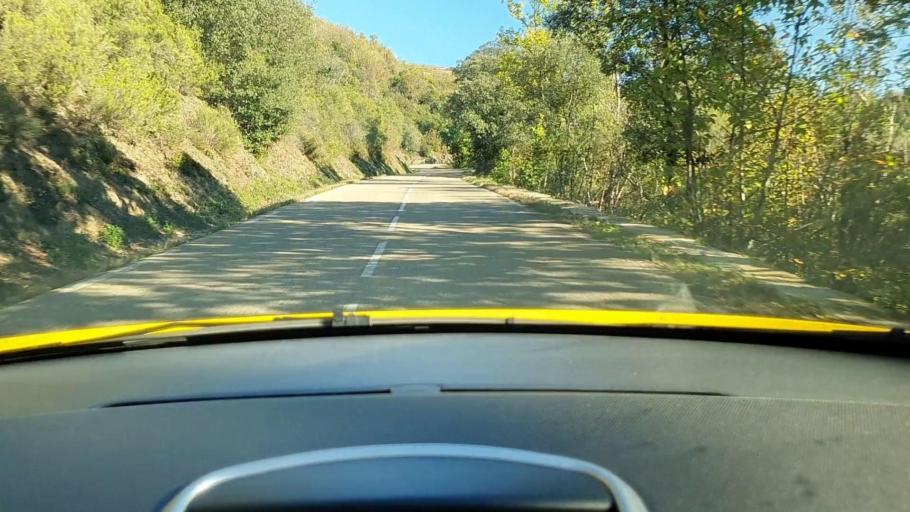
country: FR
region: Languedoc-Roussillon
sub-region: Departement du Gard
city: Sumene
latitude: 43.9893
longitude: 3.6964
